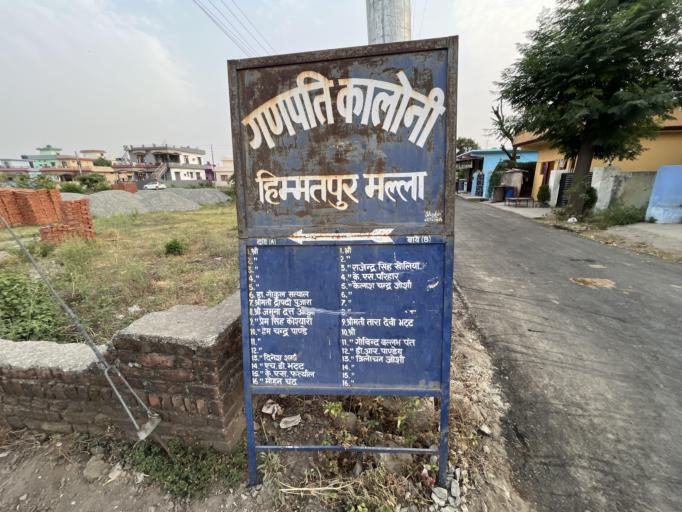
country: IN
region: Uttarakhand
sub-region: Naini Tal
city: Haldwani
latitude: 29.2220
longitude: 79.4833
